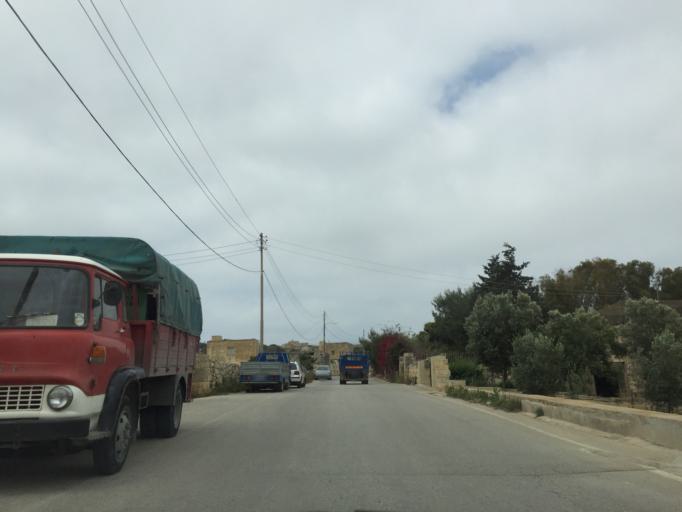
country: MT
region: Dingli
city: Dingli
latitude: 35.8807
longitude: 14.3677
